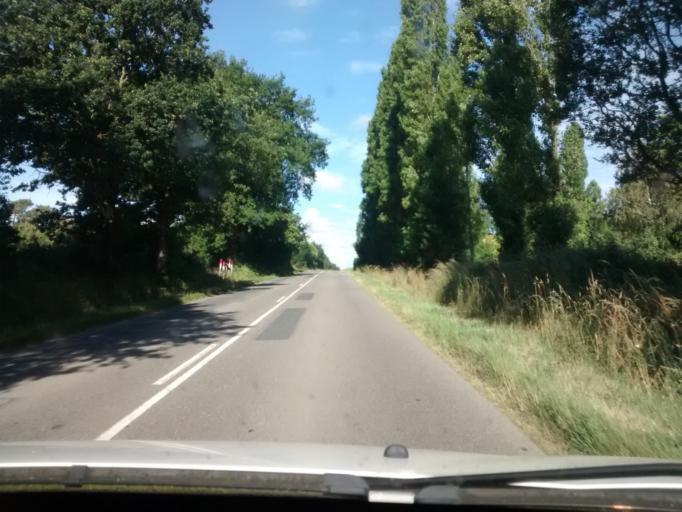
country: FR
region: Brittany
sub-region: Departement d'Ille-et-Vilaine
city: Bain-de-Bretagne
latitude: 47.8497
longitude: -1.7181
